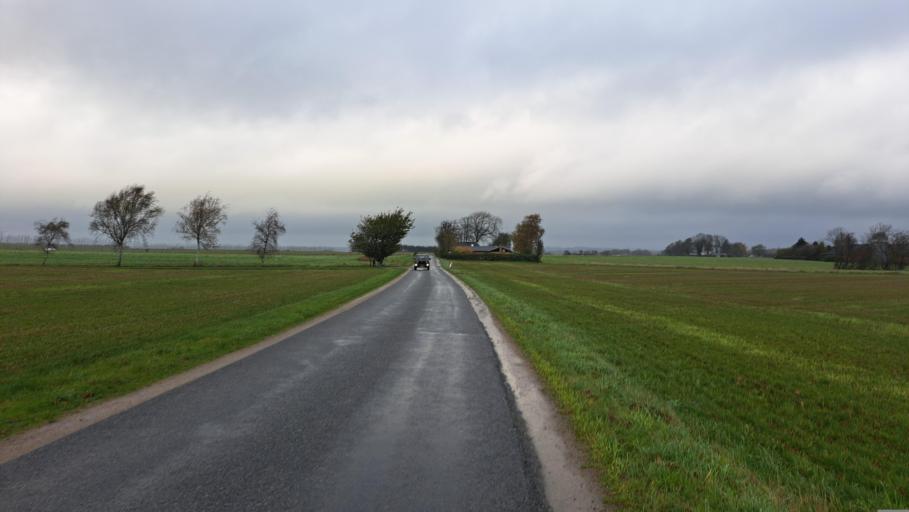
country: DK
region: Central Jutland
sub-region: Hedensted Kommune
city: Hedensted
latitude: 55.8278
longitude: 9.7320
